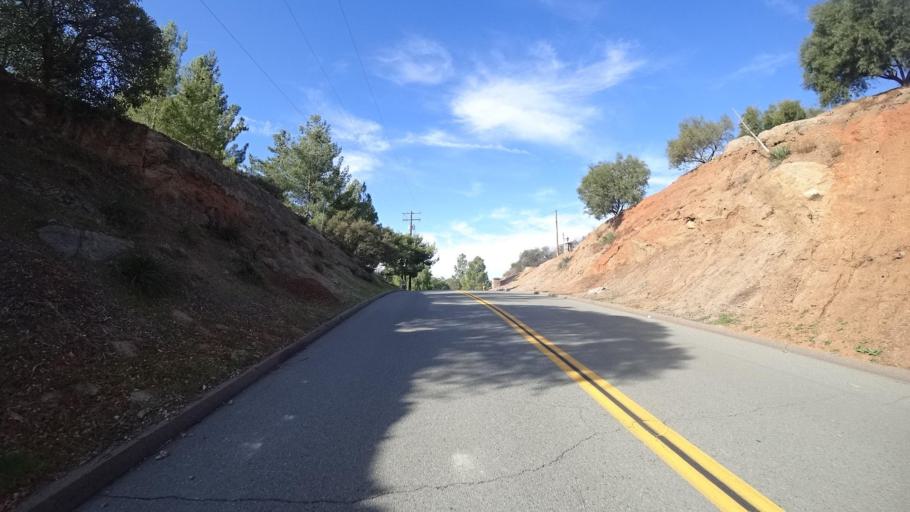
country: US
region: California
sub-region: San Diego County
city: Alpine
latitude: 32.8140
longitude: -116.7266
